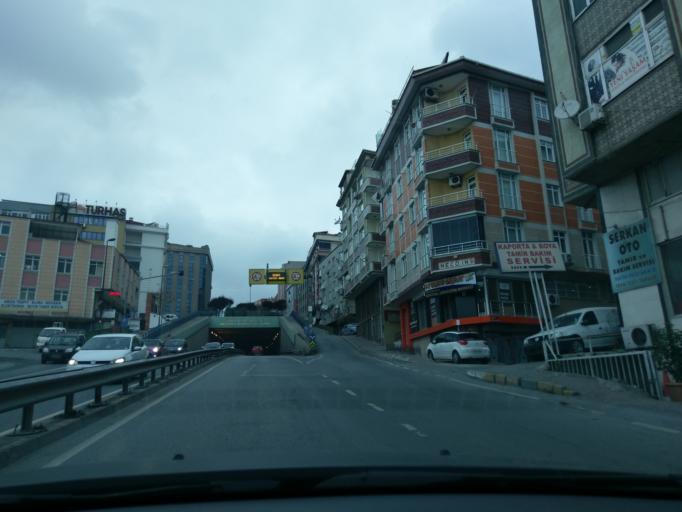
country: TR
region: Istanbul
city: Bahcelievler
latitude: 41.0138
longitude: 28.8444
